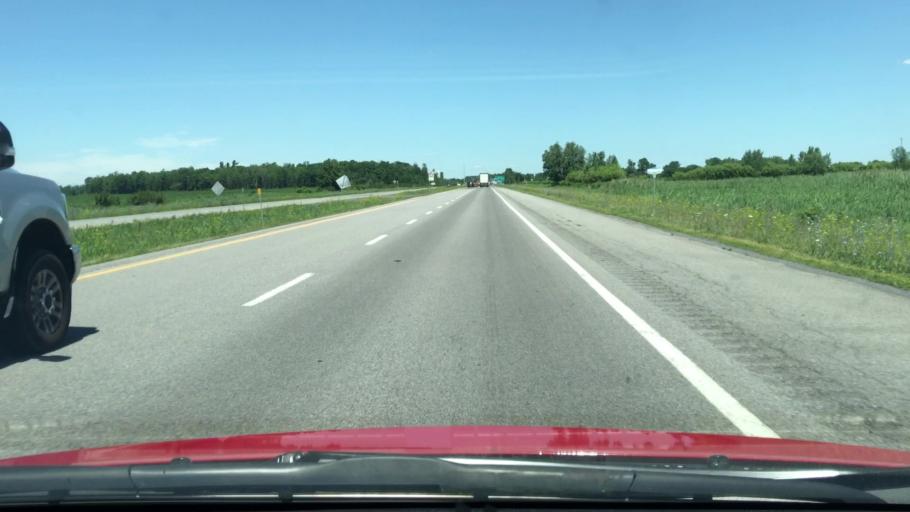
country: CA
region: Quebec
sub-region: Monteregie
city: Napierville
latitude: 45.1797
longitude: -73.4582
